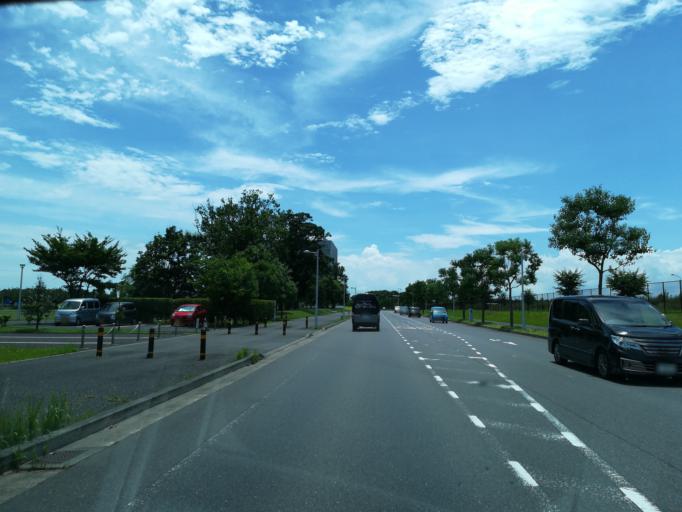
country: JP
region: Ibaraki
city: Naka
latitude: 36.0816
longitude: 140.0795
